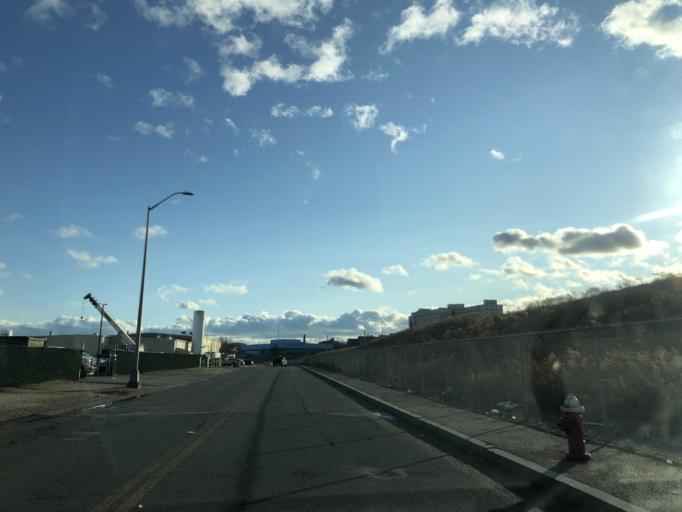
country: US
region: Massachusetts
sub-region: Bristol County
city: New Bedford
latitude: 41.6441
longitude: -70.9241
